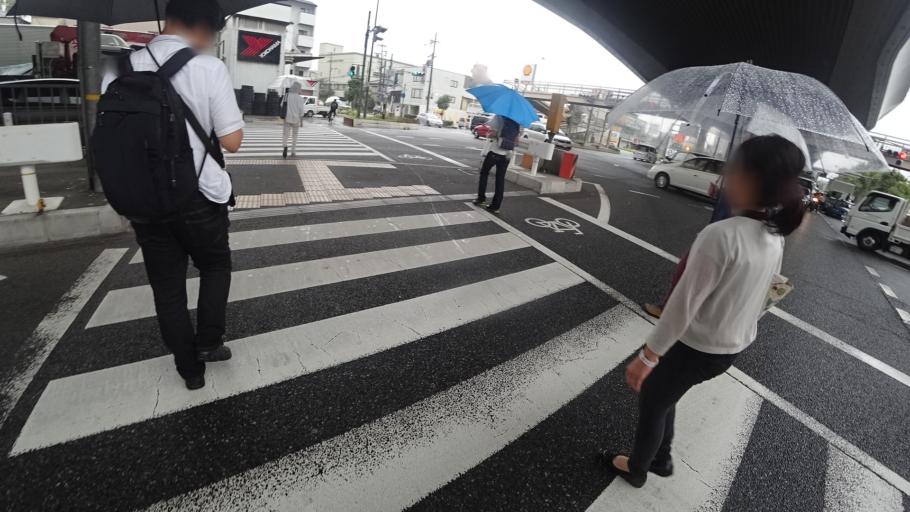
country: JP
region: Hyogo
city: Nishinomiya-hama
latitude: 34.7338
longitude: 135.3360
